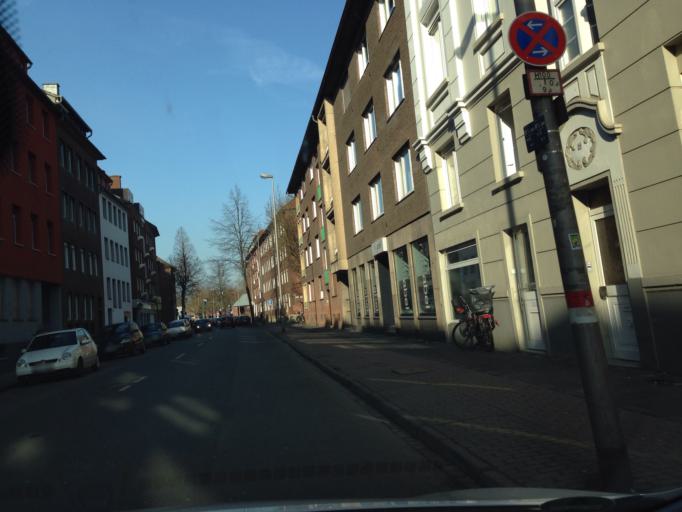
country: DE
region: North Rhine-Westphalia
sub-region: Regierungsbezirk Munster
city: Muenster
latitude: 51.9542
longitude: 7.6371
